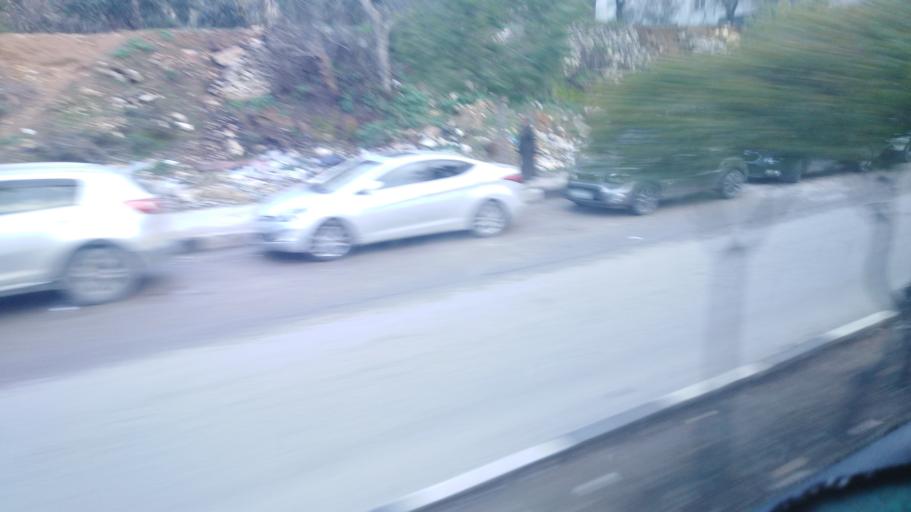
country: PS
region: West Bank
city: Hebron
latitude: 31.5292
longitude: 35.0951
